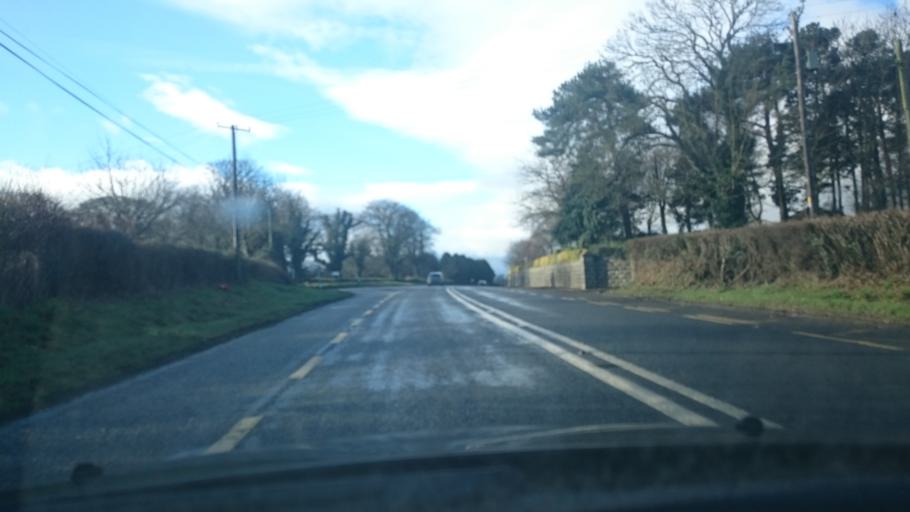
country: IE
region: Leinster
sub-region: Kilkenny
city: Callan
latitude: 52.5667
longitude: -7.3478
